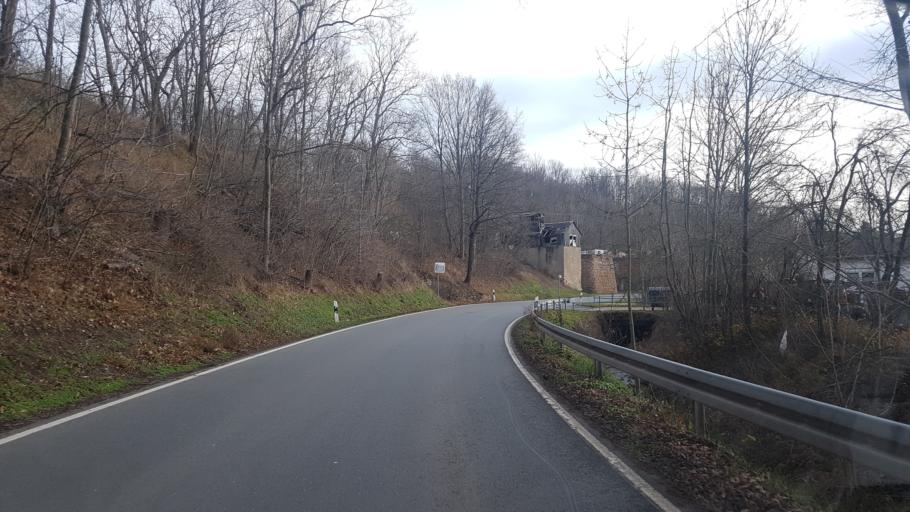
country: DE
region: Saxony
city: Ostrau
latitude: 51.1939
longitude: 13.1663
